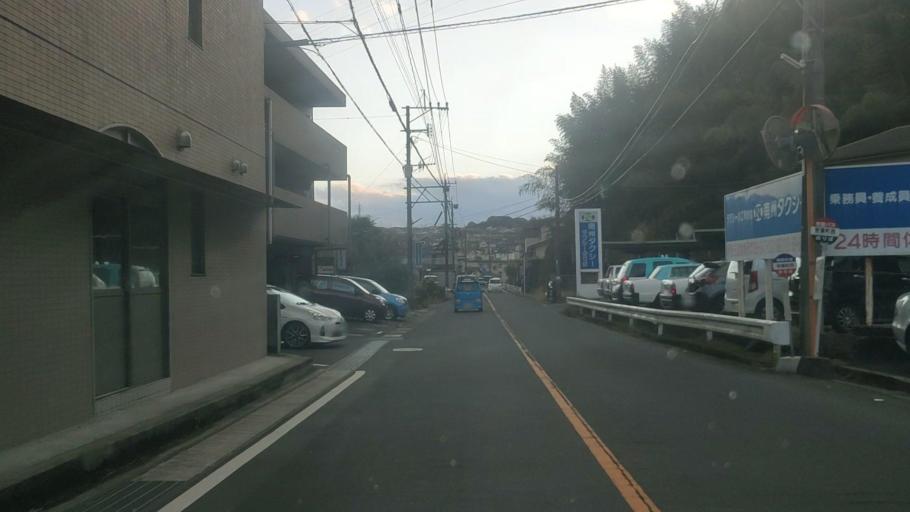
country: JP
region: Kagoshima
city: Kagoshima-shi
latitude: 31.6251
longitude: 130.5430
